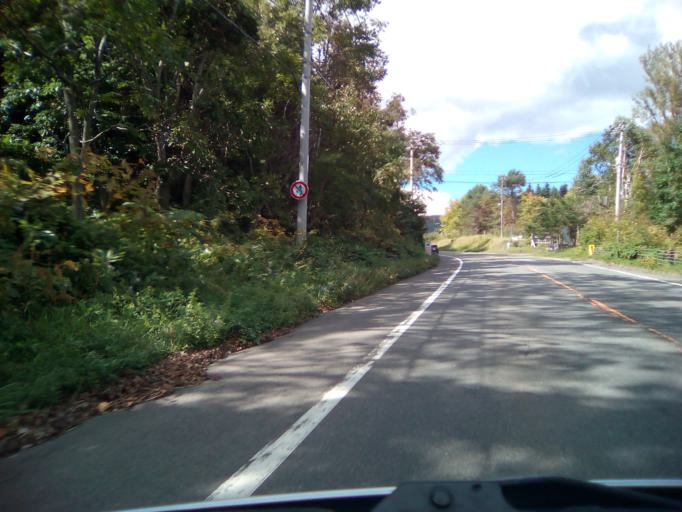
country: JP
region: Hokkaido
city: Date
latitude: 42.5889
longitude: 140.7921
